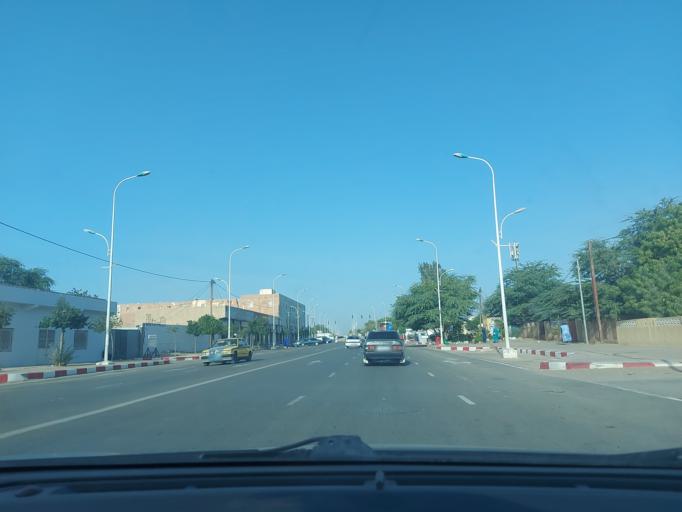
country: MR
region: Nouakchott
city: Nouakchott
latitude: 18.0873
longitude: -15.9847
